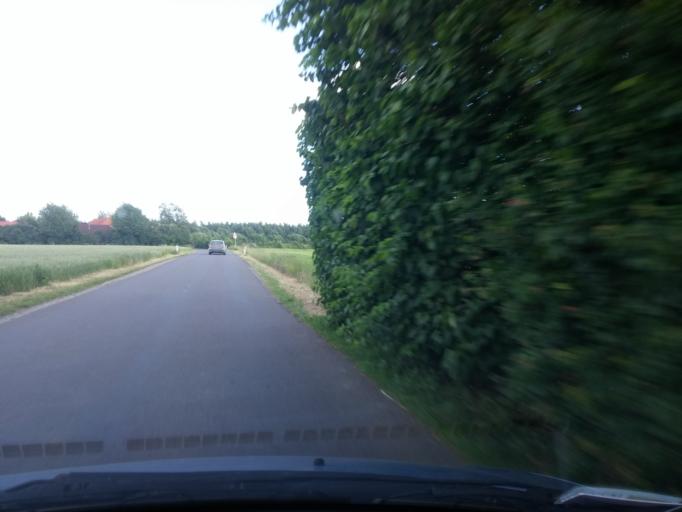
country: DK
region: South Denmark
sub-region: Kerteminde Kommune
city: Langeskov
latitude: 55.3949
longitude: 10.5579
